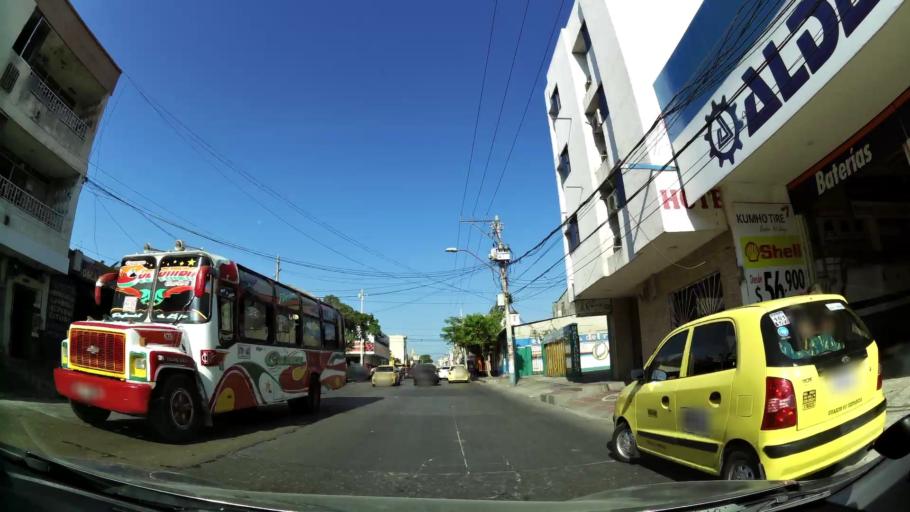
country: CO
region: Atlantico
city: Barranquilla
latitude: 10.9800
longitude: -74.7877
